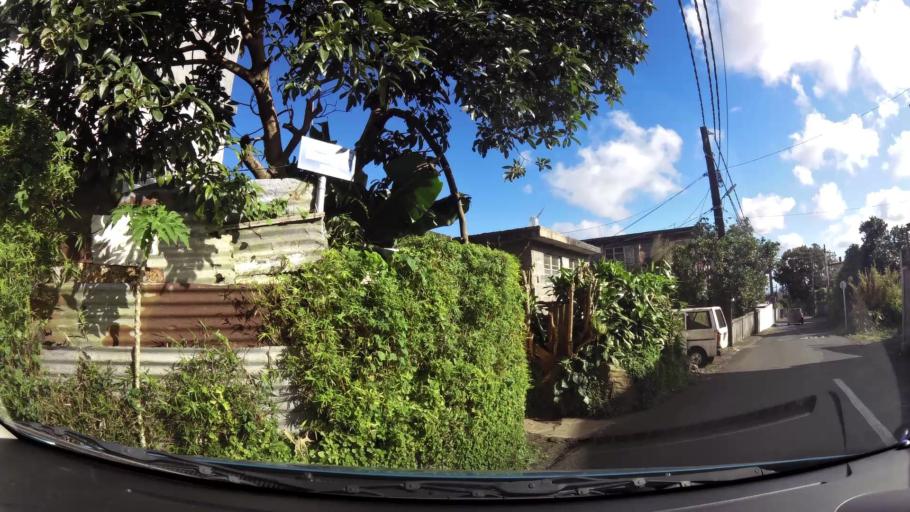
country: MU
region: Plaines Wilhems
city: Curepipe
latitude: -20.3076
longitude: 57.5179
